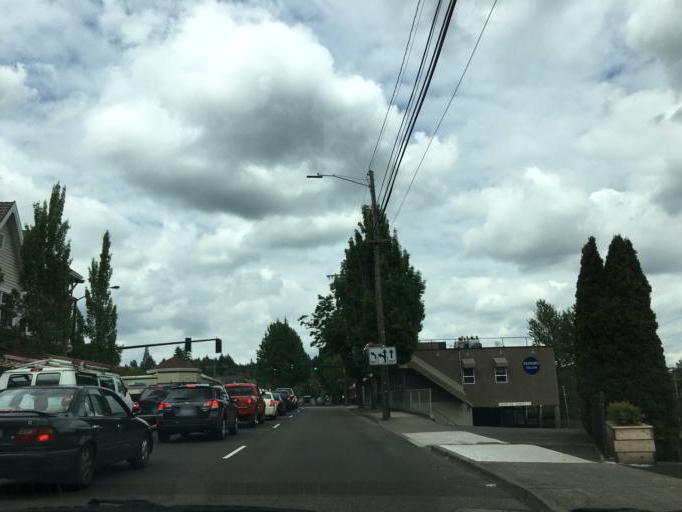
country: US
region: Oregon
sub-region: Clackamas County
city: Lake Oswego
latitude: 45.4185
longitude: -122.6630
